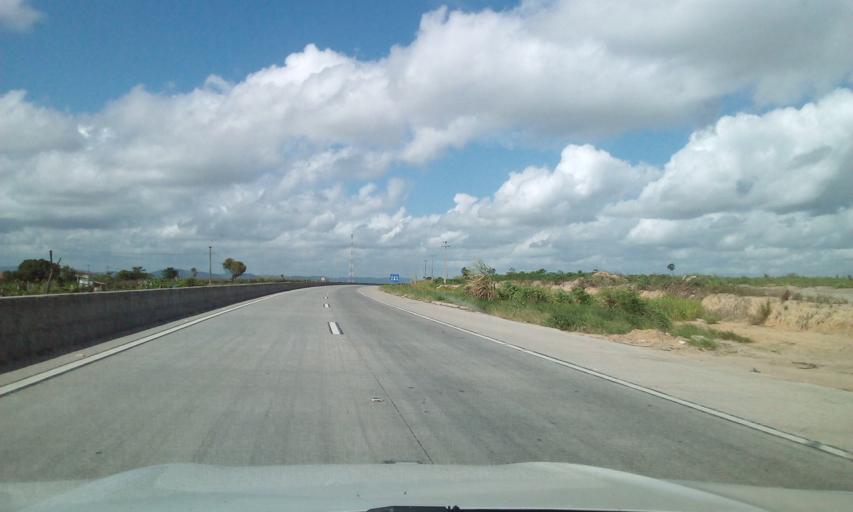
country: BR
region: Alagoas
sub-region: Messias
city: Messias
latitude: -9.3937
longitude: -35.8362
